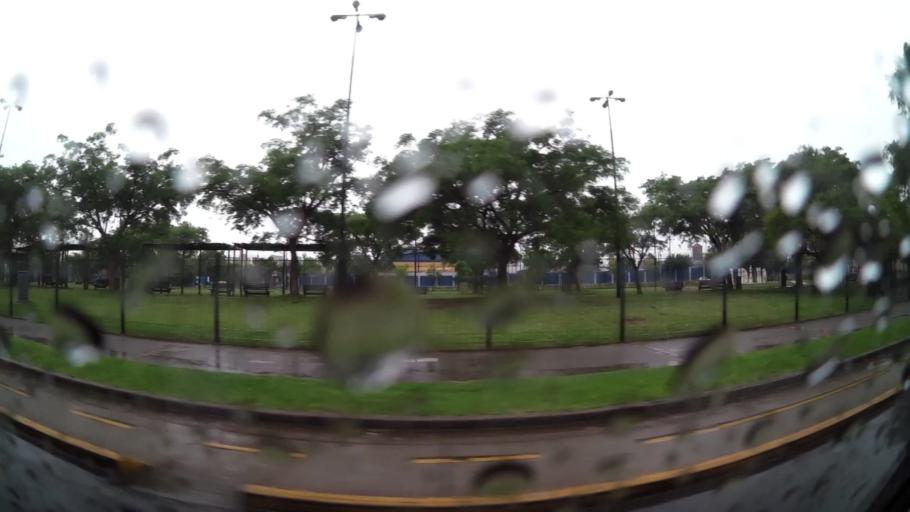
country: AR
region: Buenos Aires F.D.
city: Buenos Aires
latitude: -34.6332
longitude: -58.3676
